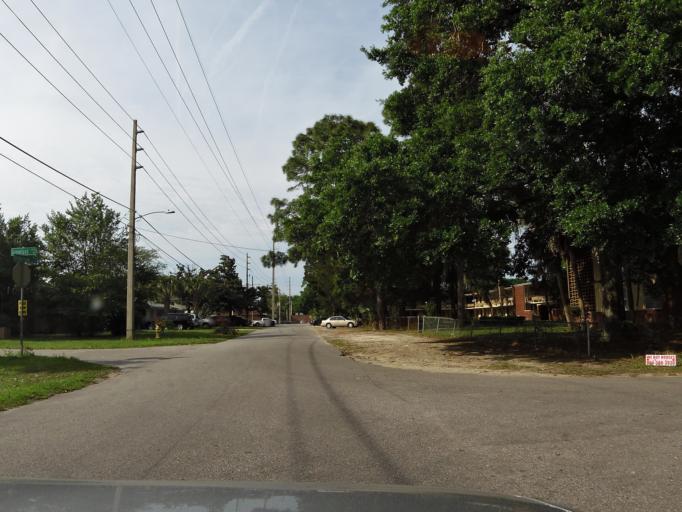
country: US
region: Florida
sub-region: Duval County
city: Jacksonville
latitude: 30.3324
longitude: -81.5915
